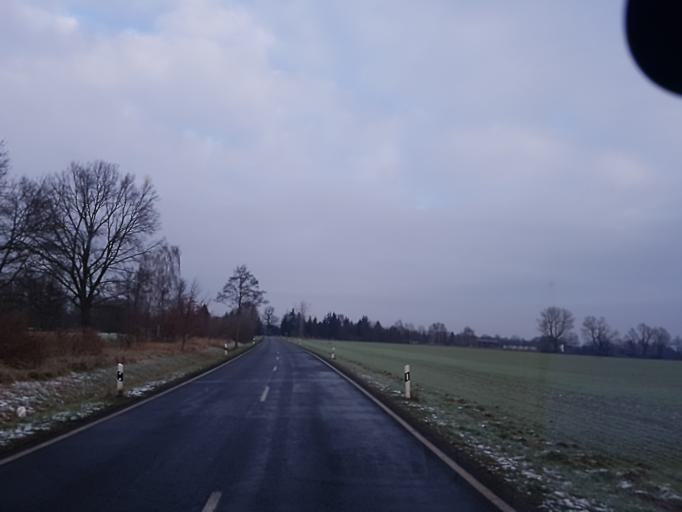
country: DE
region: Brandenburg
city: Calau
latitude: 51.7564
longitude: 13.8595
